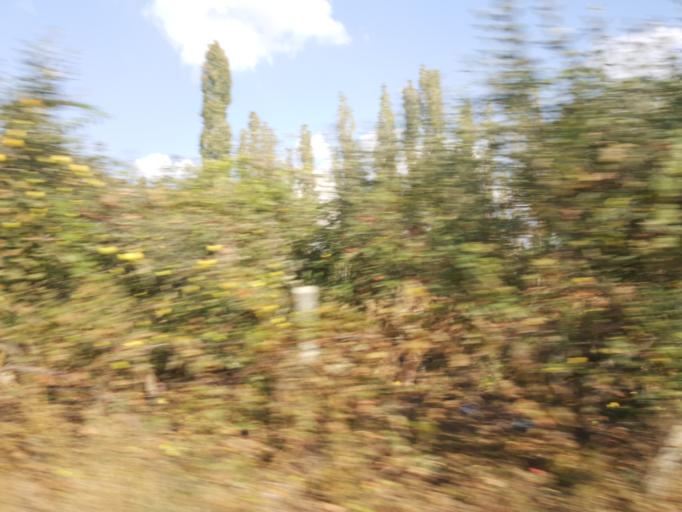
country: TR
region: Corum
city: Sungurlu
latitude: 40.1821
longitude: 34.4915
